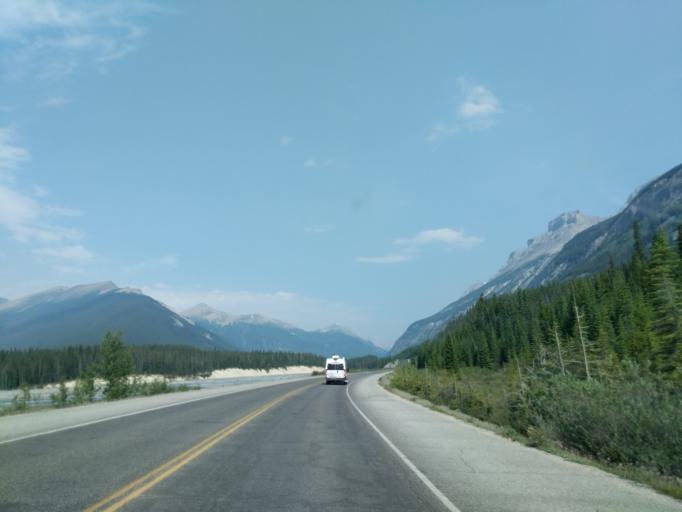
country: CA
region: British Columbia
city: Golden
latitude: 52.0698
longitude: -116.9162
